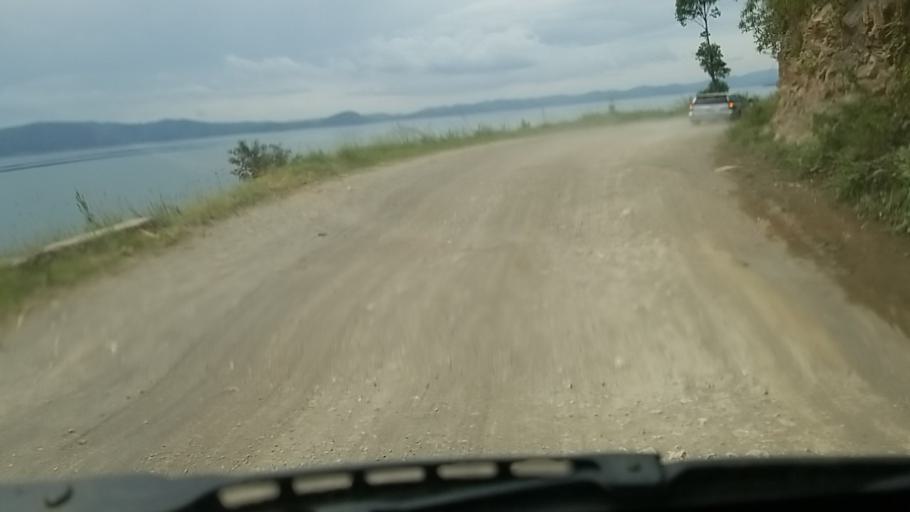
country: CD
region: Nord Kivu
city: Sake
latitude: -1.5886
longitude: 29.0463
